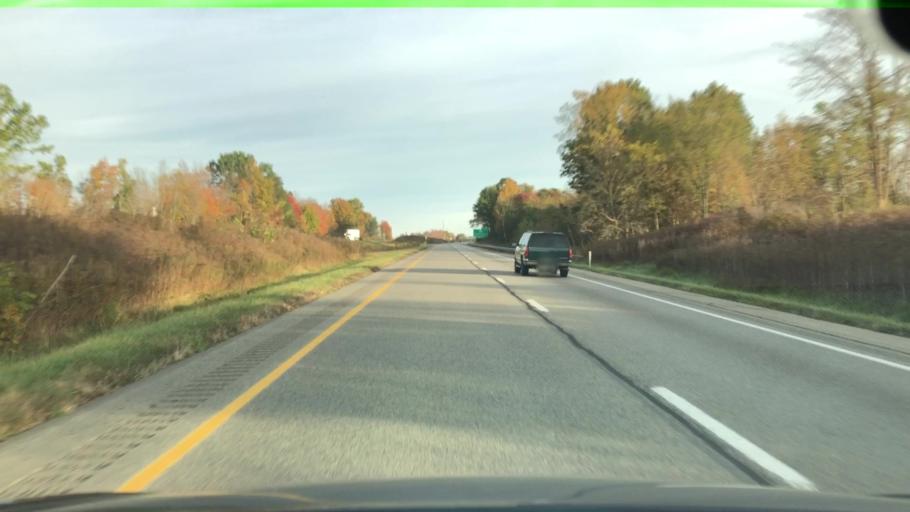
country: US
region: Pennsylvania
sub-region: Mercer County
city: Stoneboro
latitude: 41.3772
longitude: -80.1580
